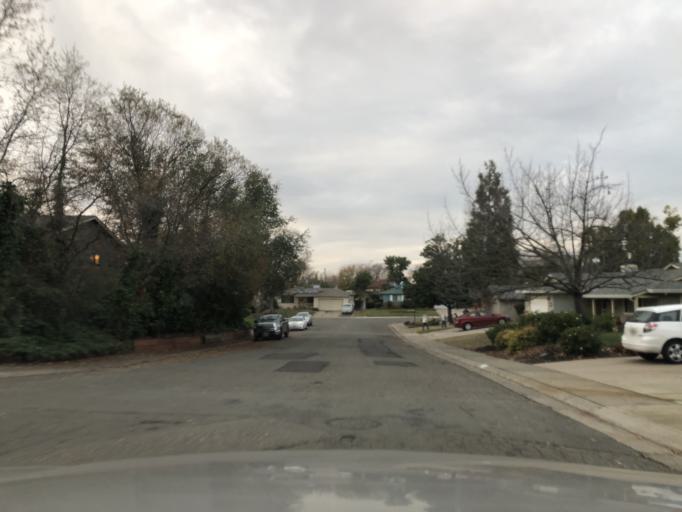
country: US
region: California
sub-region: Sacramento County
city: Fair Oaks
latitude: 38.6583
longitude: -121.3101
